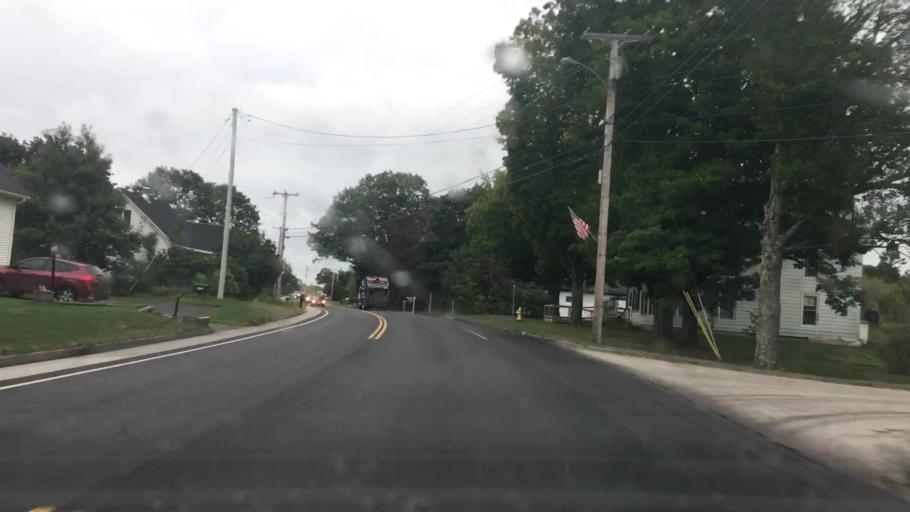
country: US
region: Maine
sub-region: Penobscot County
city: Orrington
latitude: 44.7487
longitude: -68.8068
